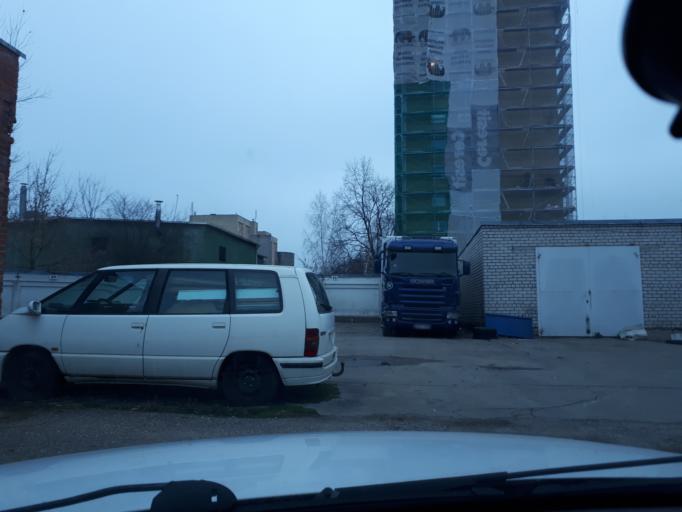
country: LT
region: Kauno apskritis
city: Dainava (Kaunas)
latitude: 54.9164
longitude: 23.9487
